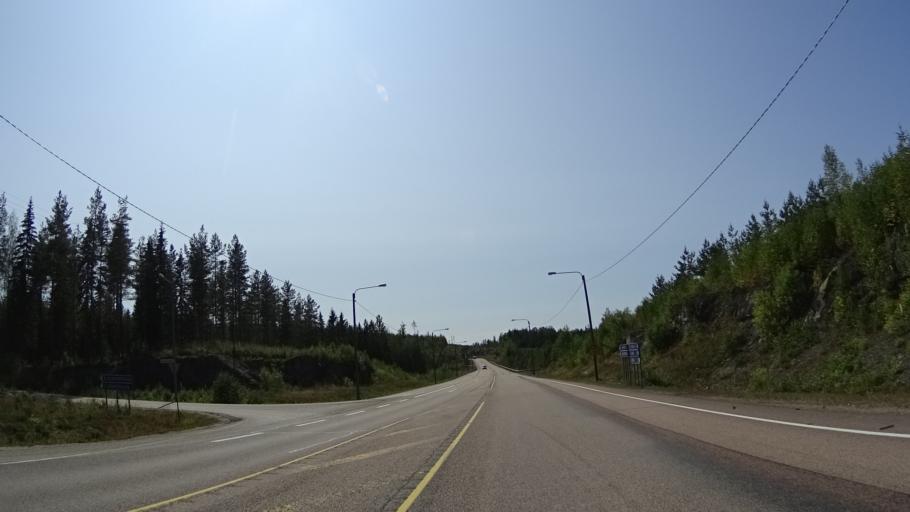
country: FI
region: Central Finland
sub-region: Jaemsae
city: Jaemsae
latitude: 61.7756
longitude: 24.8904
